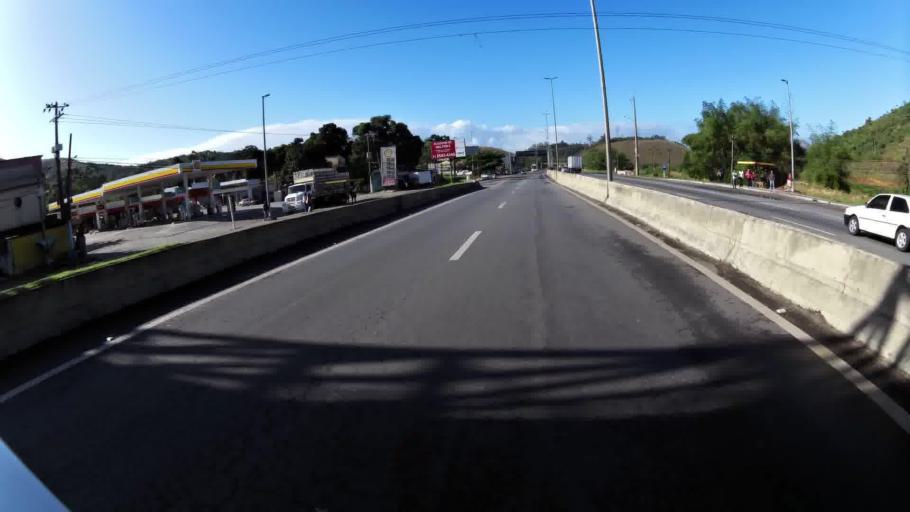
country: BR
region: Rio de Janeiro
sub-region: Petropolis
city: Petropolis
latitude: -22.6154
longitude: -43.2867
